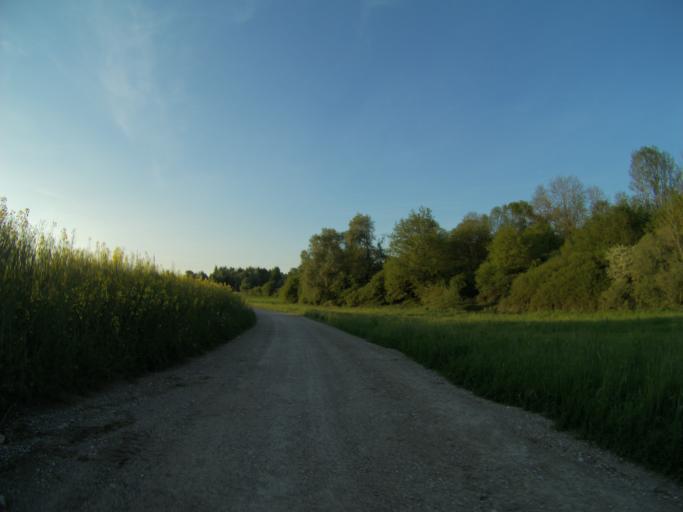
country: DE
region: Bavaria
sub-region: Upper Bavaria
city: Marzling
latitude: 48.4129
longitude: 11.7857
